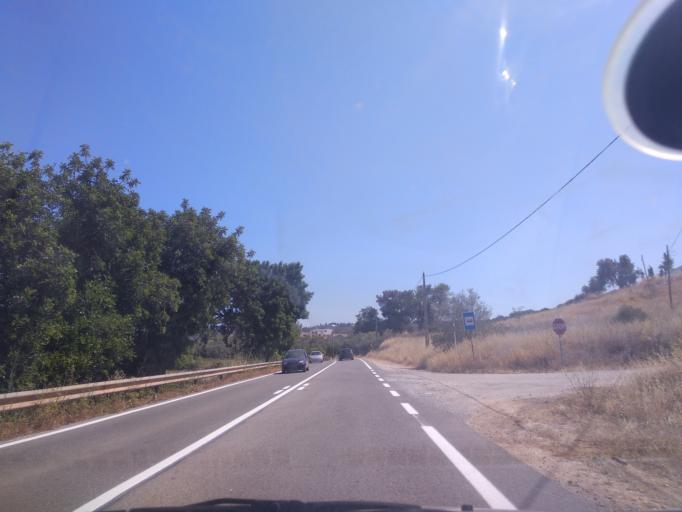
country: PT
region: Faro
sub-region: Lagos
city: Lagos
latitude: 37.1309
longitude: -8.6971
